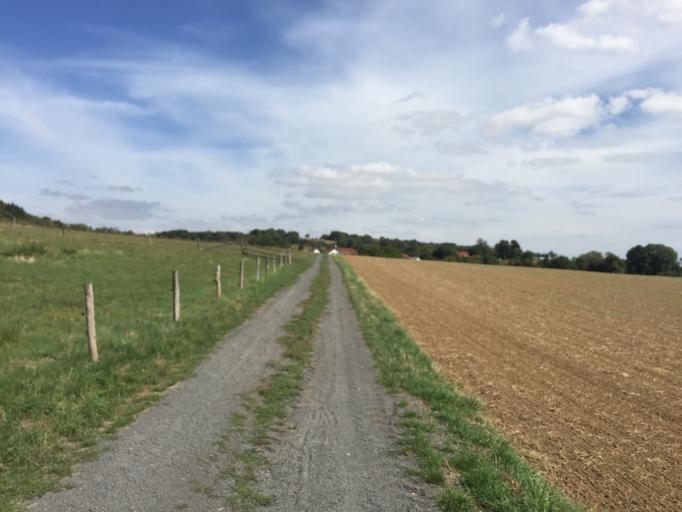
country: DE
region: Hesse
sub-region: Regierungsbezirk Giessen
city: Reiskirchen
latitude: 50.5986
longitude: 8.8897
